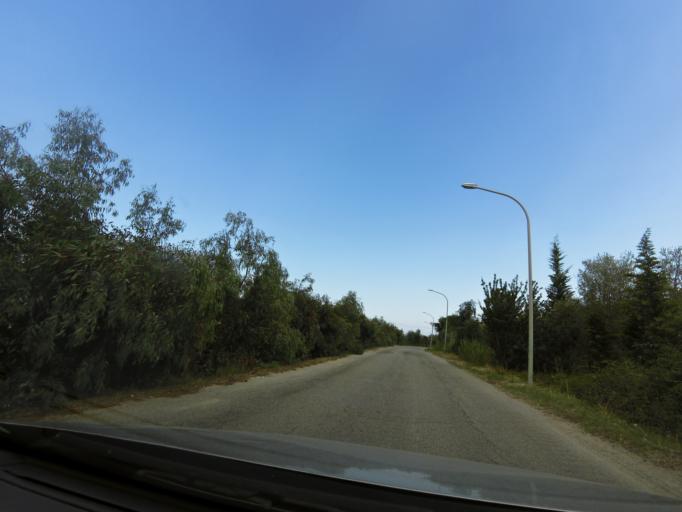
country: IT
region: Calabria
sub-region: Provincia di Reggio Calabria
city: Monasterace Marina
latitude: 38.4213
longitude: 16.5577
